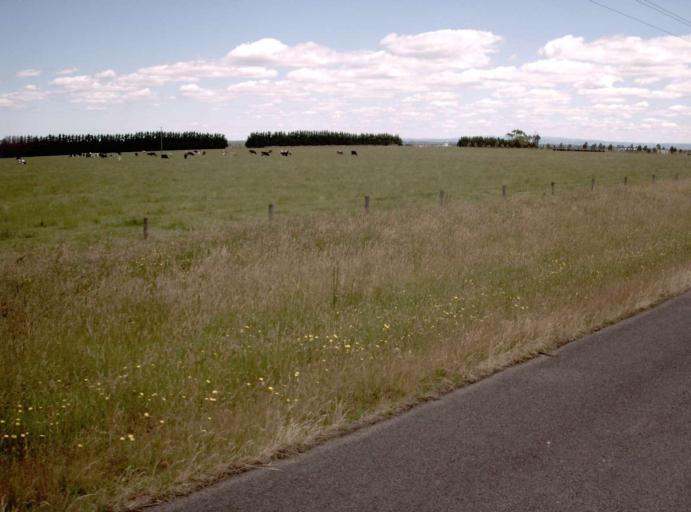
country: AU
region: Victoria
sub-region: Cardinia
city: Koo-Wee-Rup
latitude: -38.3067
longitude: 145.5418
